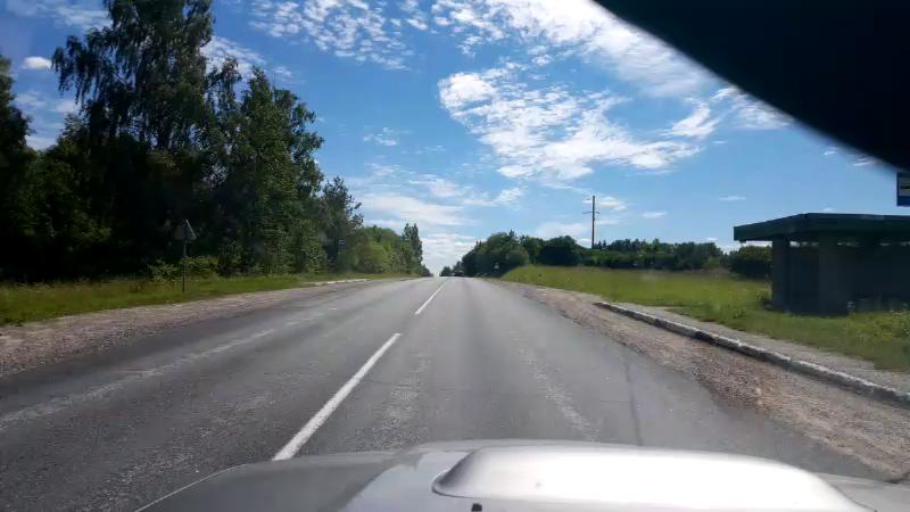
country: EE
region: Laeaene-Virumaa
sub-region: Rakke vald
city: Rakke
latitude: 58.8492
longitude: 26.2912
